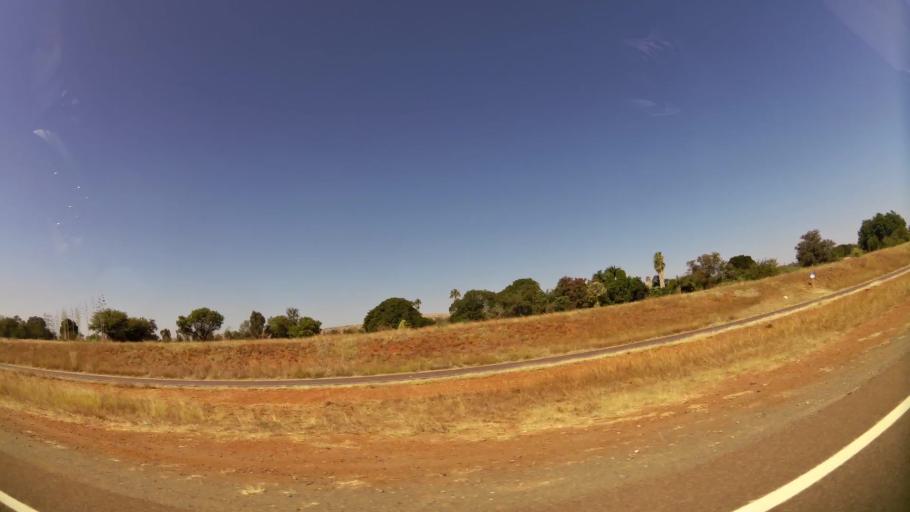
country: ZA
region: North-West
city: Ga-Rankuwa
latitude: -25.6572
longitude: 28.0796
